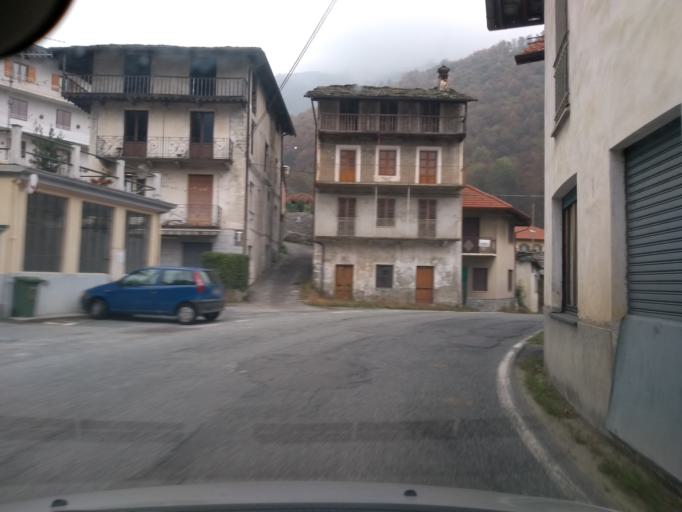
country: IT
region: Piedmont
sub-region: Provincia di Torino
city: Ceres
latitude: 45.3070
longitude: 7.3965
